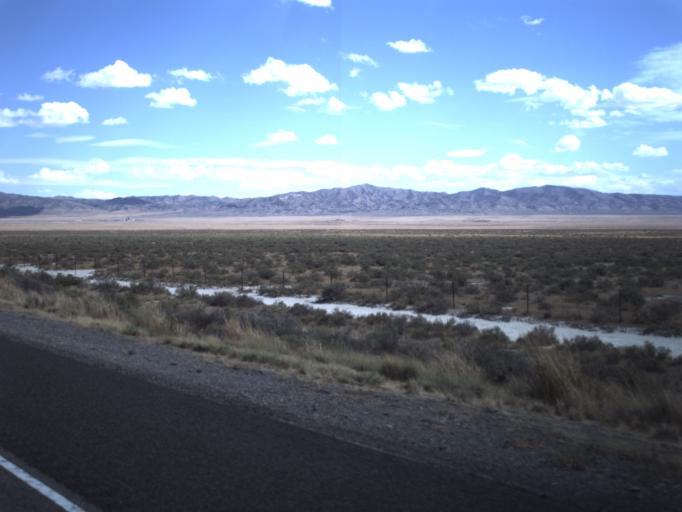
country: US
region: Utah
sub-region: Tooele County
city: Grantsville
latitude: 40.7397
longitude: -113.0840
